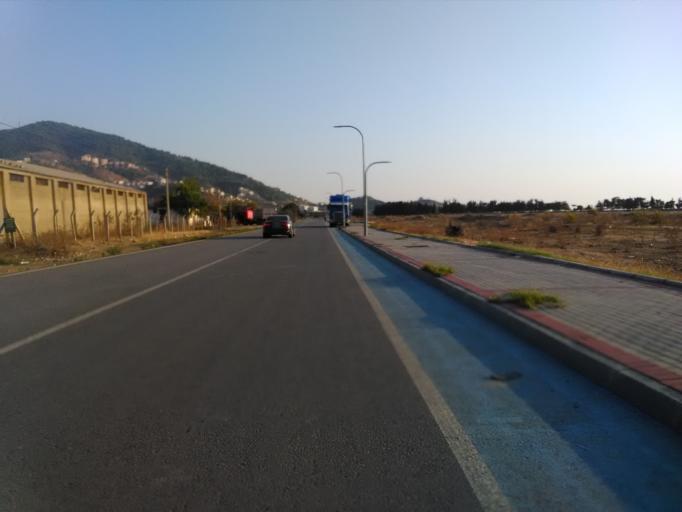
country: TR
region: Antalya
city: Gazipasa
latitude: 36.2491
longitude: 32.2939
